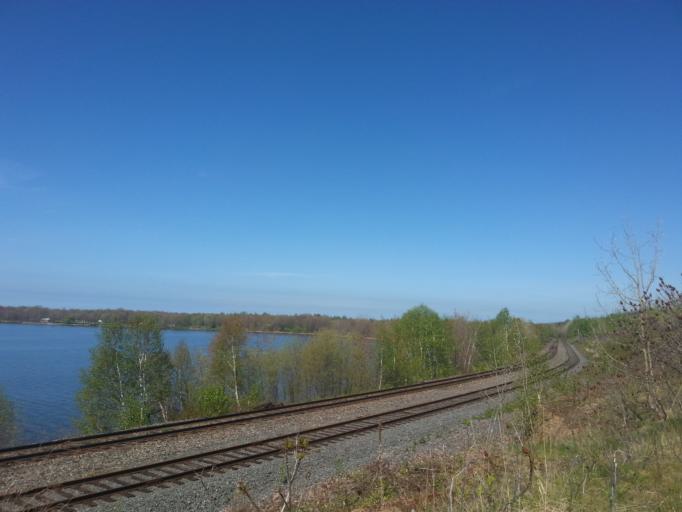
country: CA
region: Ontario
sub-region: Nipissing District
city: North Bay
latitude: 46.3549
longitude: -79.6483
